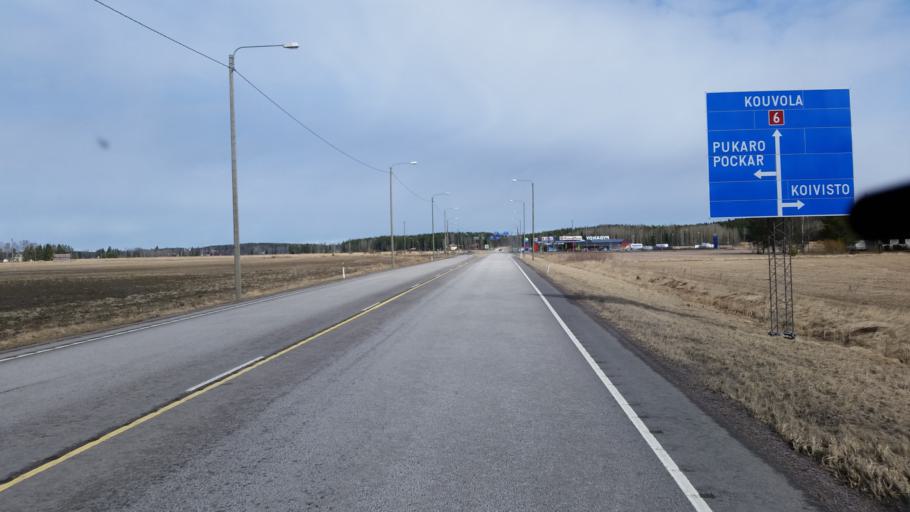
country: FI
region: Uusimaa
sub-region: Loviisa
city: Lapinjaervi
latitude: 60.6676
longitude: 26.2489
